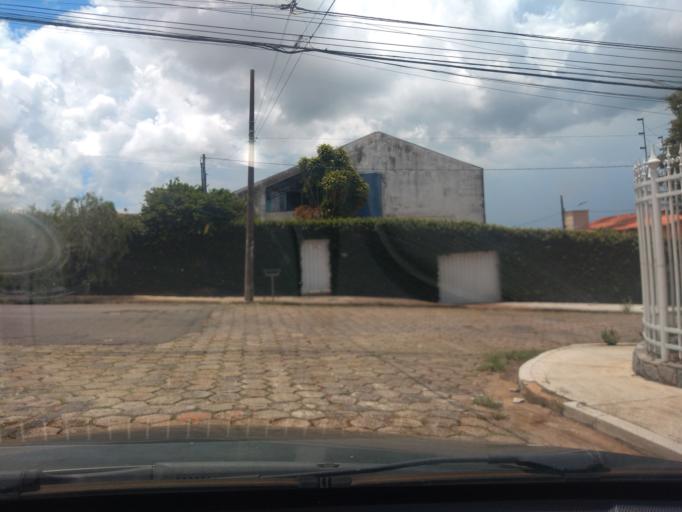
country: BR
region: Minas Gerais
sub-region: Tres Coracoes
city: Tres Coracoes
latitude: -21.6892
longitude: -45.2625
